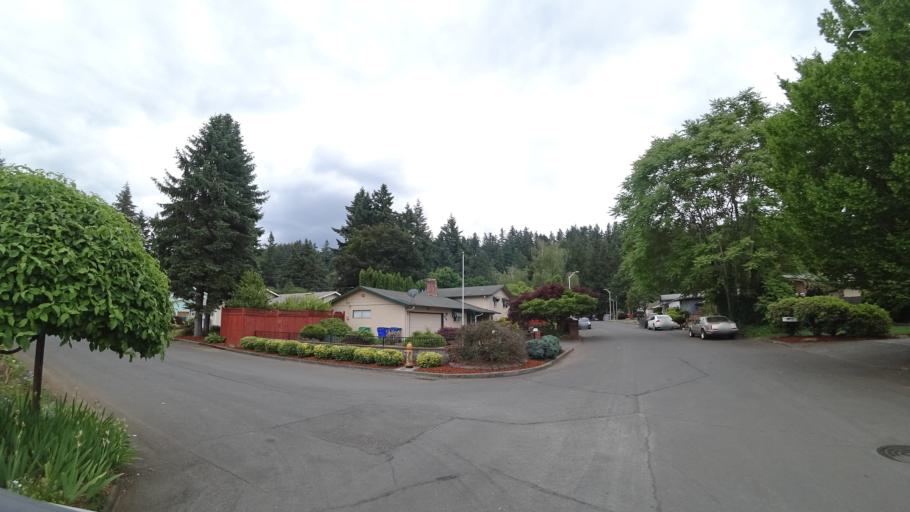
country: US
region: Oregon
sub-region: Clackamas County
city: Happy Valley
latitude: 45.4953
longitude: -122.5086
